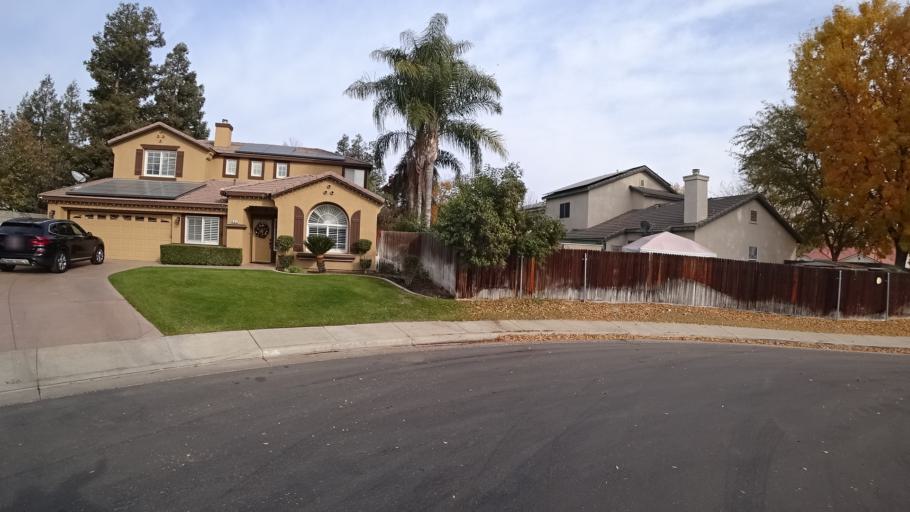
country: US
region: California
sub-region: Kern County
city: Rosedale
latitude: 35.3471
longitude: -119.1339
